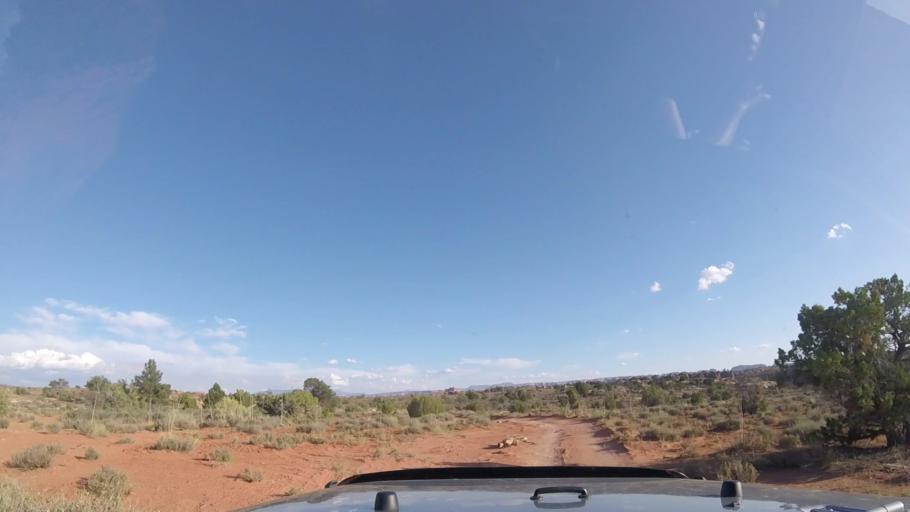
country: US
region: Utah
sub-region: Grand County
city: Moab
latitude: 38.2097
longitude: -109.7877
